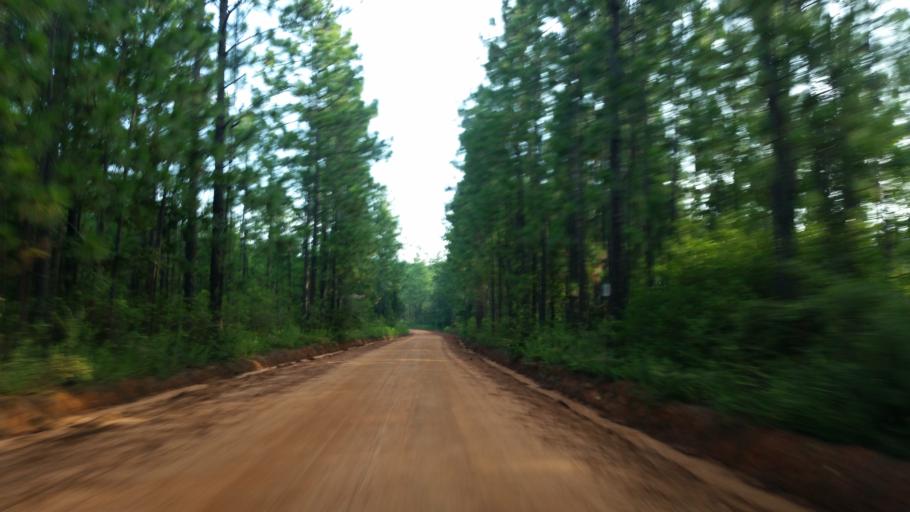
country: US
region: Alabama
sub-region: Escambia County
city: Atmore
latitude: 30.9412
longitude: -87.5714
